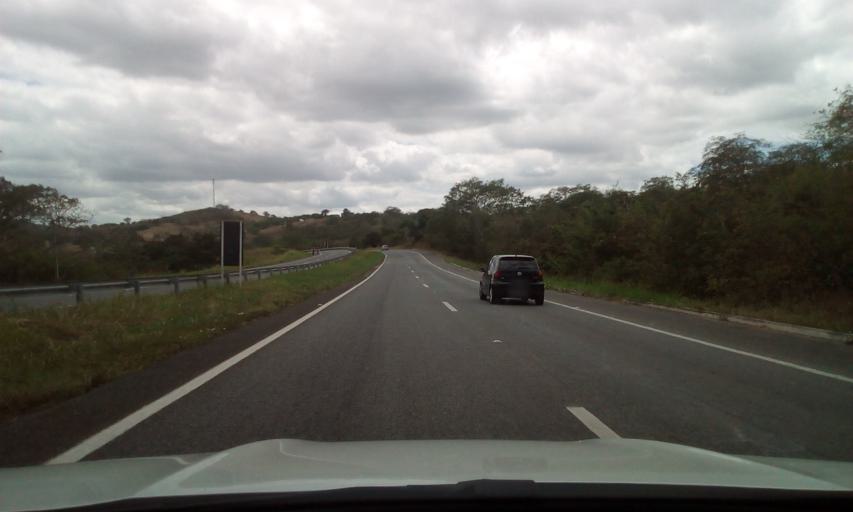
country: BR
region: Paraiba
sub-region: Fagundes
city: Fagundes
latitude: -7.2818
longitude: -35.7657
